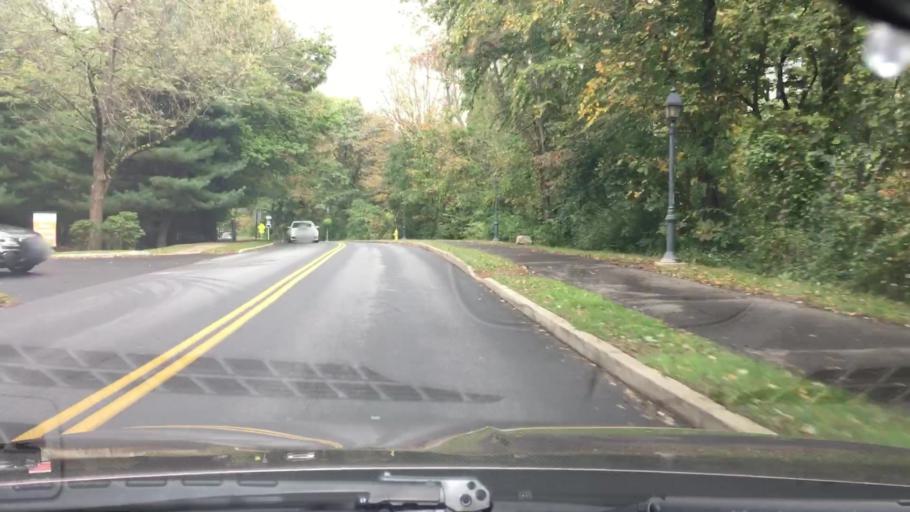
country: US
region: Connecticut
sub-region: Fairfield County
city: Wilton
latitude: 41.1882
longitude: -73.4299
